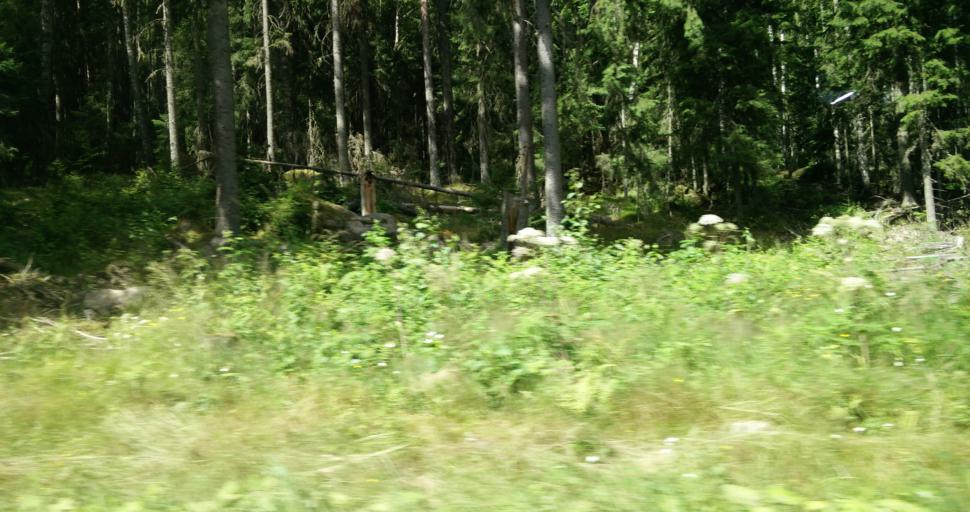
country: SE
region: Vaermland
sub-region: Hagfors Kommun
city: Ekshaerad
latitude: 60.0956
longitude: 13.4498
